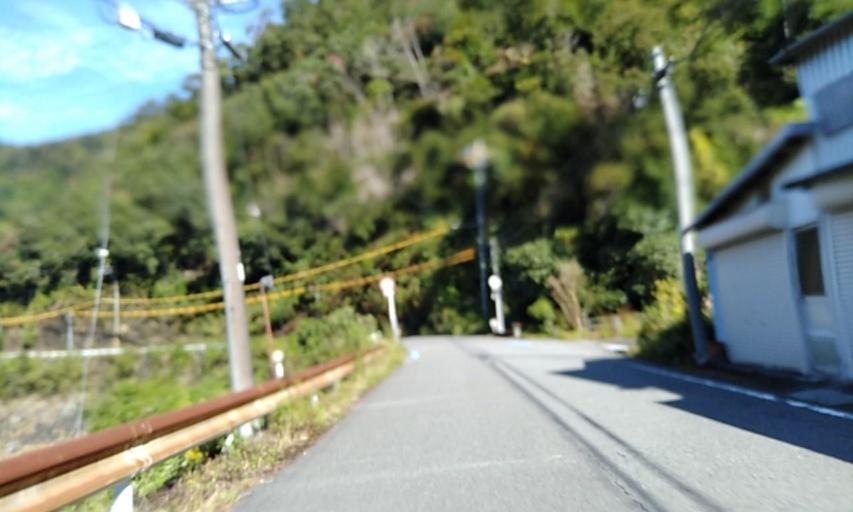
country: JP
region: Wakayama
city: Kainan
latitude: 34.0541
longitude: 135.3413
